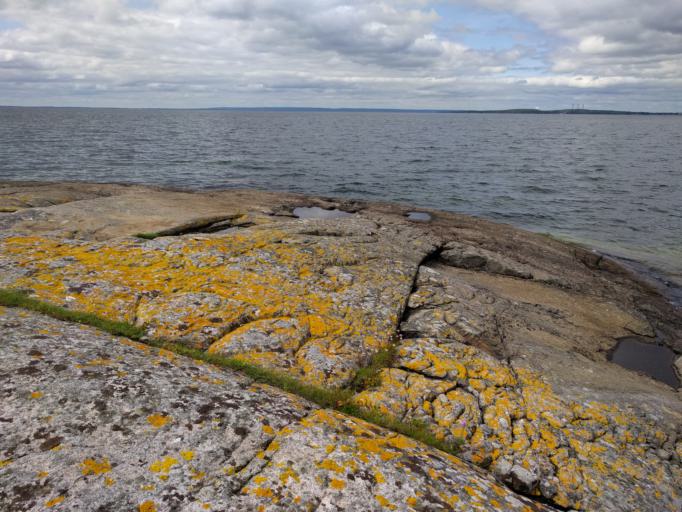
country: SE
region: Blekinge
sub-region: Karlshamns Kommun
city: Karlshamn
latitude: 56.1232
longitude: 14.9535
